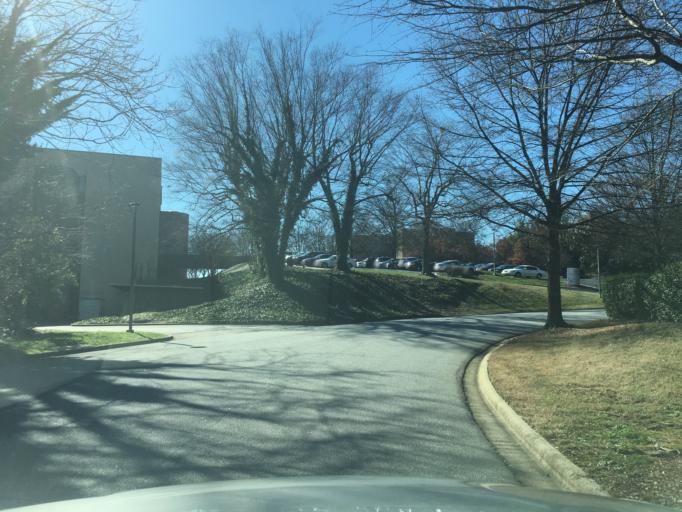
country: US
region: South Carolina
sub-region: Greenville County
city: Wade Hampton
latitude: 34.8572
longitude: -82.3388
